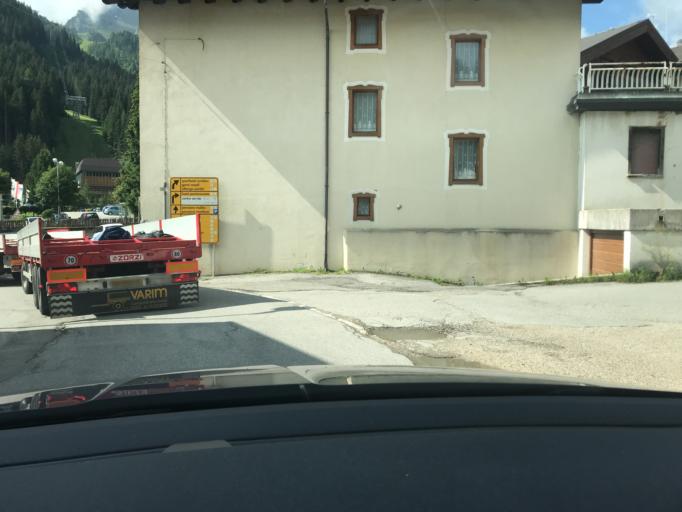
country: IT
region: Trentino-Alto Adige
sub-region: Bolzano
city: Corvara in Badia
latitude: 46.4981
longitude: 11.8744
